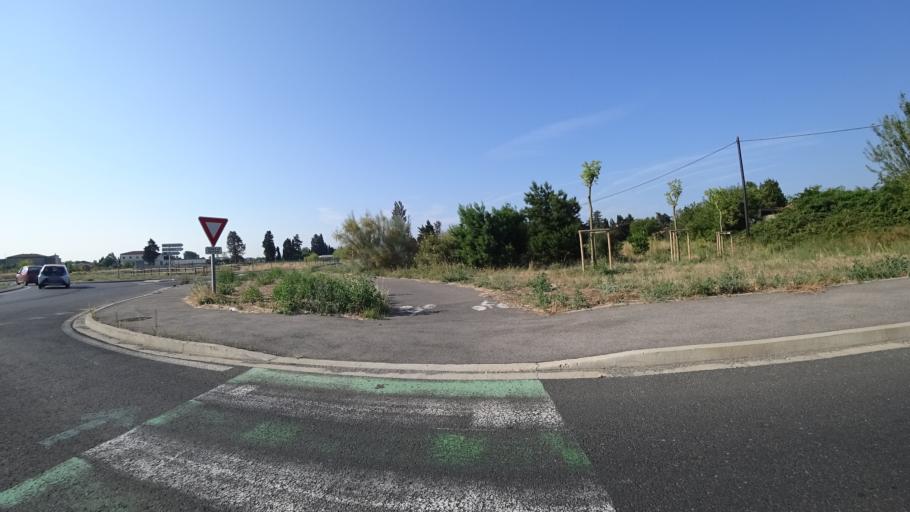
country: FR
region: Languedoc-Roussillon
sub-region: Departement des Pyrenees-Orientales
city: Perpignan
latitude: 42.7134
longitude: 2.9053
